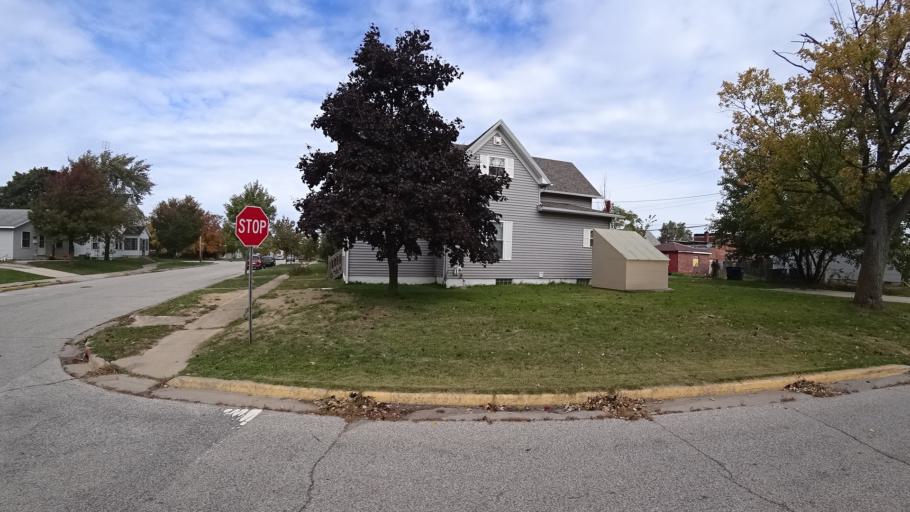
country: US
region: Indiana
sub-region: LaPorte County
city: Michigan City
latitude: 41.7058
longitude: -86.9052
